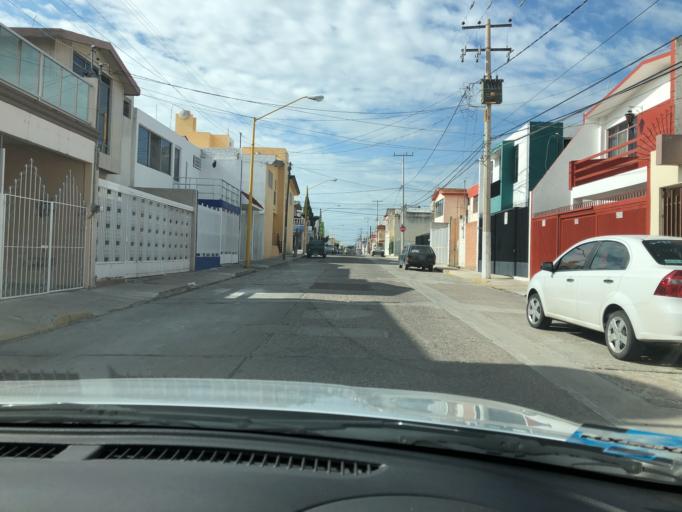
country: MX
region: Aguascalientes
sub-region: Aguascalientes
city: Aguascalientes
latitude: 21.8707
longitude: -102.3046
